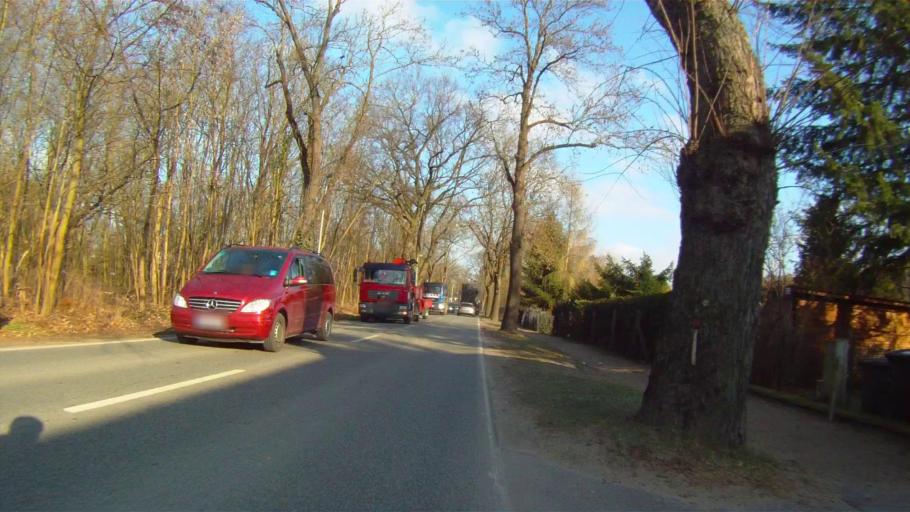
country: DE
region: Brandenburg
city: Woltersdorf
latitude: 52.4585
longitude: 13.7566
